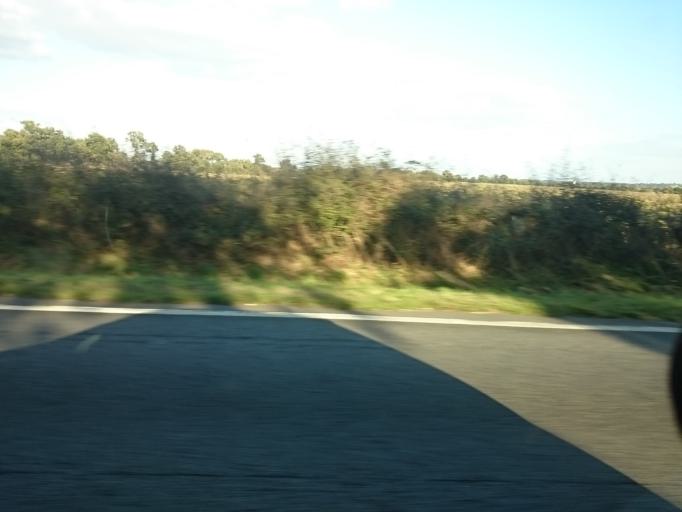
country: FR
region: Brittany
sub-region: Departement d'Ille-et-Vilaine
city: Grand-Fougeray
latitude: 47.7134
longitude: -1.7068
